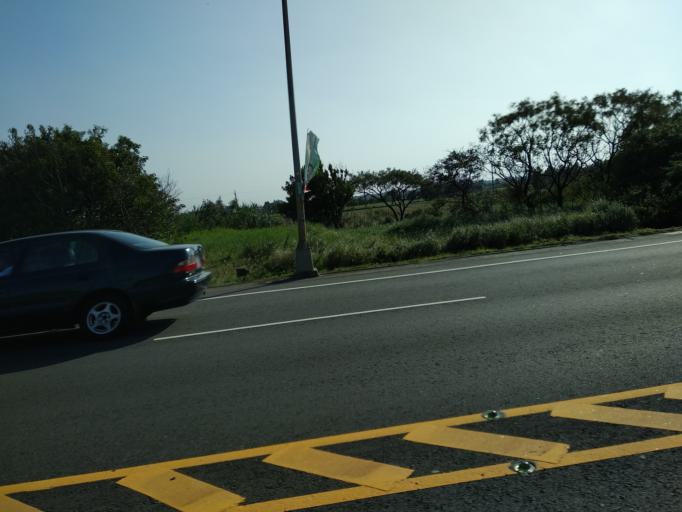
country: TW
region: Taiwan
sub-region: Hsinchu
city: Zhubei
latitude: 24.9825
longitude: 121.0616
